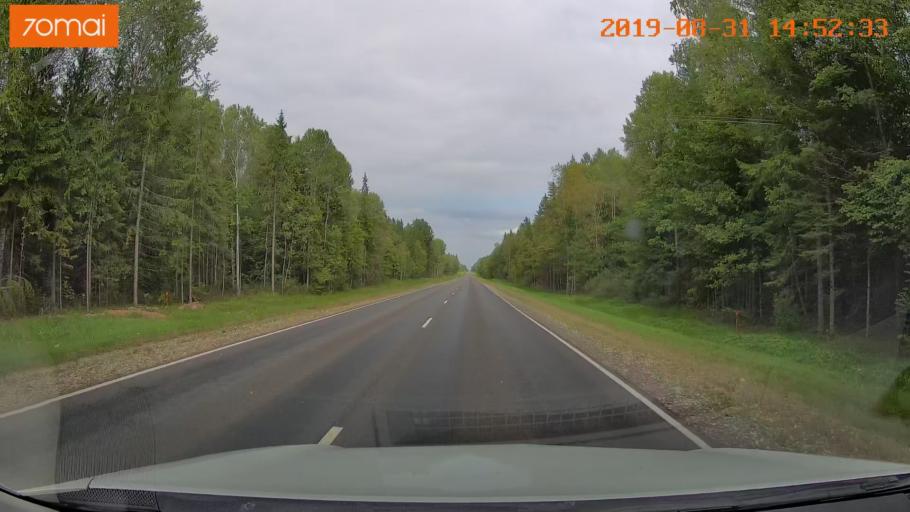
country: RU
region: Kaluga
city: Spas-Demensk
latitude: 54.2768
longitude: 33.8422
